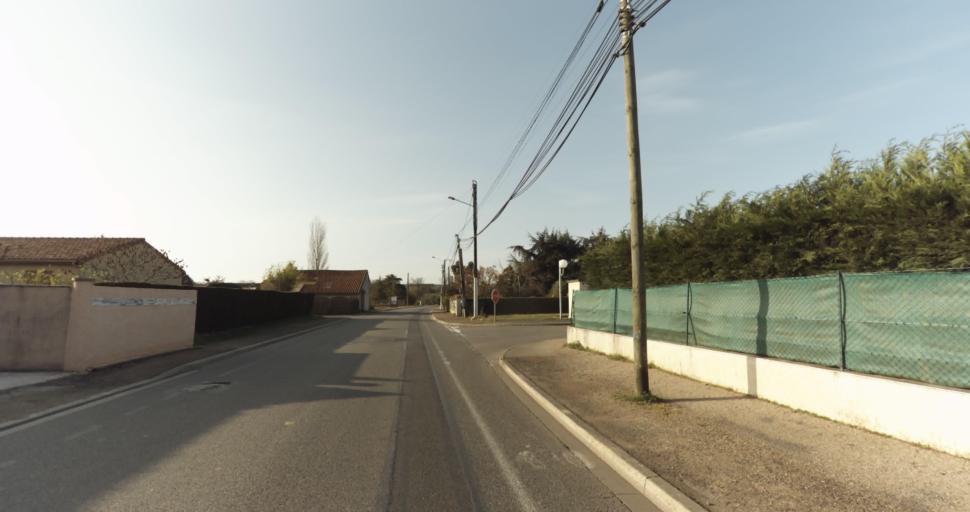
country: FR
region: Midi-Pyrenees
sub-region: Departement du Tarn
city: Saint-Sulpice-la-Pointe
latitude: 43.7652
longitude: 1.6879
